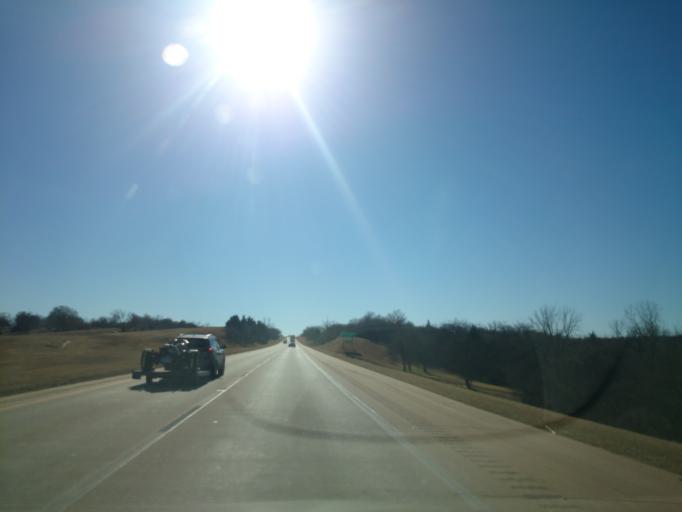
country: US
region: Oklahoma
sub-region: Logan County
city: Guthrie
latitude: 35.7767
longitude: -97.4164
